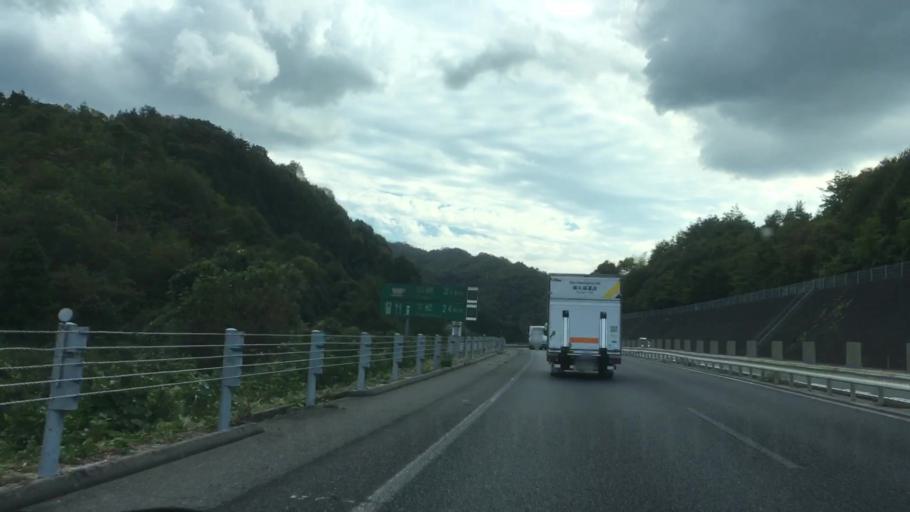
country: JP
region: Yamaguchi
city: Iwakuni
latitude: 34.1272
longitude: 132.1112
